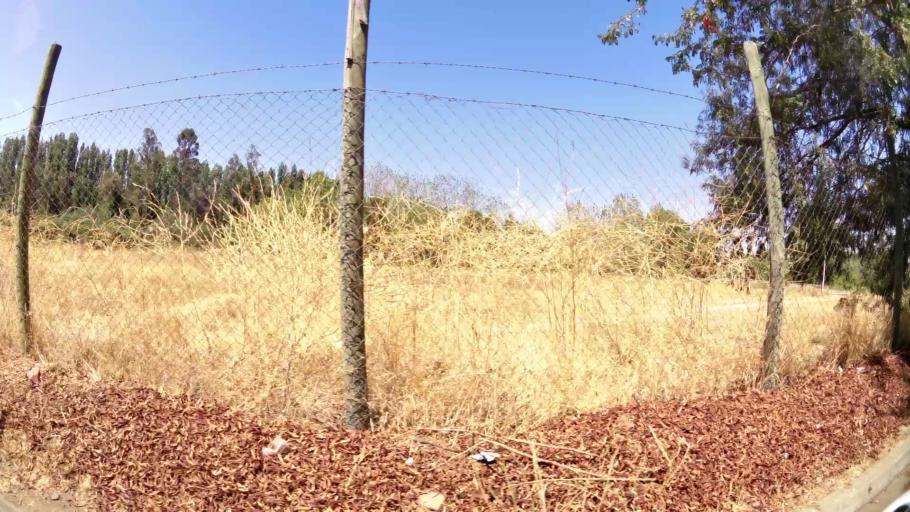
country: CL
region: Maule
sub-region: Provincia de Talca
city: Talca
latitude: -35.3079
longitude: -71.5100
